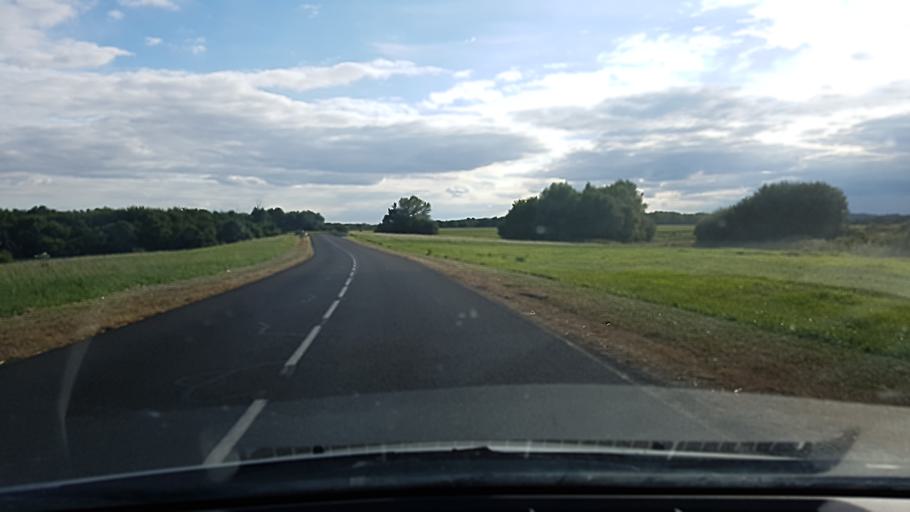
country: FR
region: Pays de la Loire
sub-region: Departement de Maine-et-Loire
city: Maze
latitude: 47.4945
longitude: -0.2708
